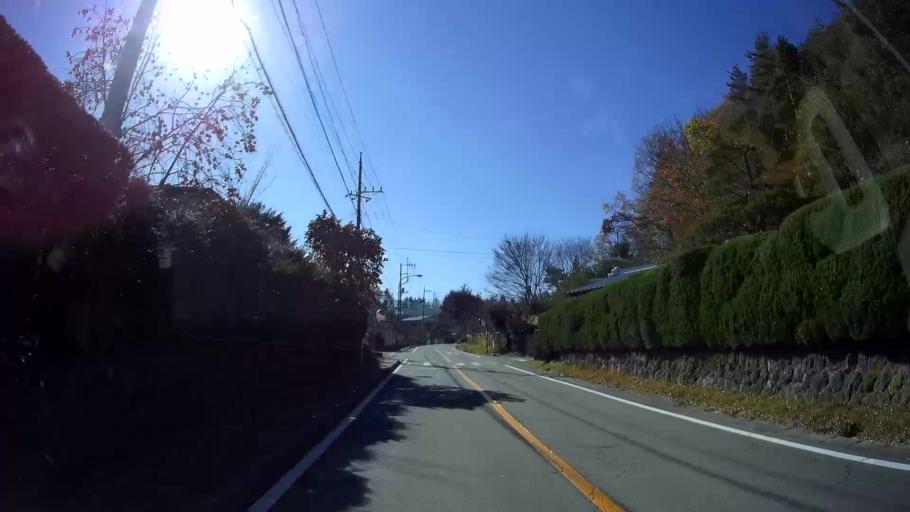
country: JP
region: Yamanashi
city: Fujikawaguchiko
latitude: 35.4950
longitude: 138.7312
